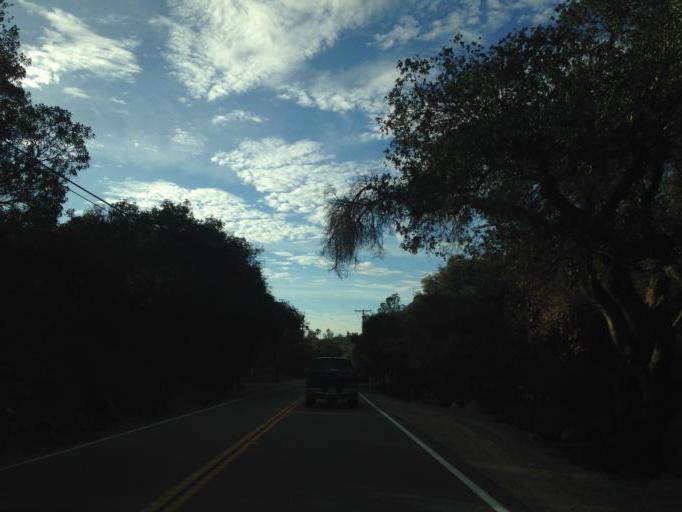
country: US
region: California
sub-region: San Diego County
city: Rainbow
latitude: 33.4186
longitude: -117.0874
